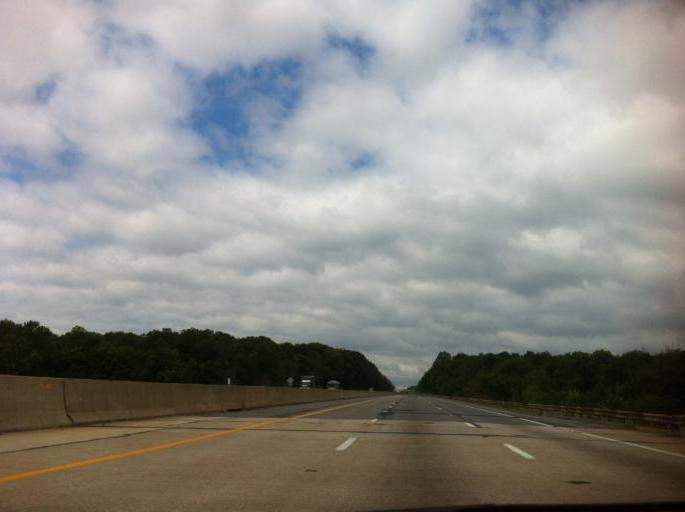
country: US
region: Ohio
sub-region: Portage County
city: Windham
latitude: 41.2424
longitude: -81.0659
